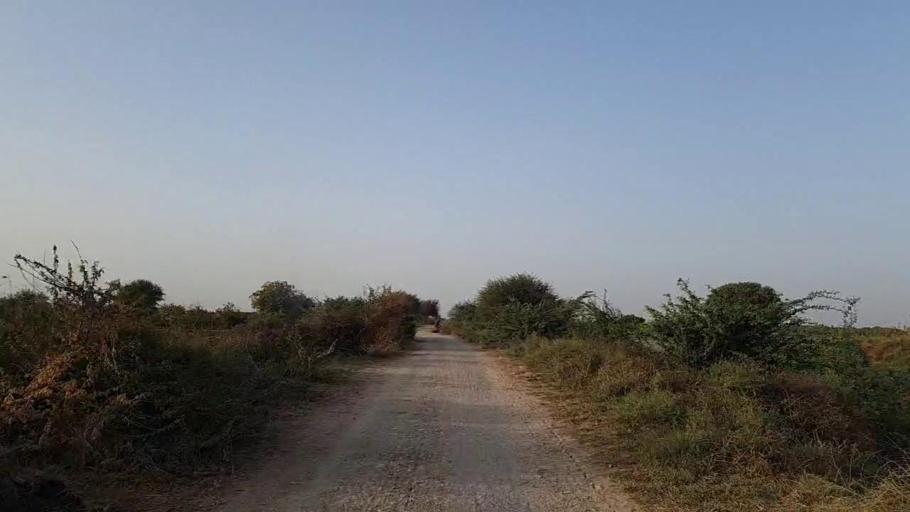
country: PK
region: Sindh
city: Jati
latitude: 24.4090
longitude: 68.1857
